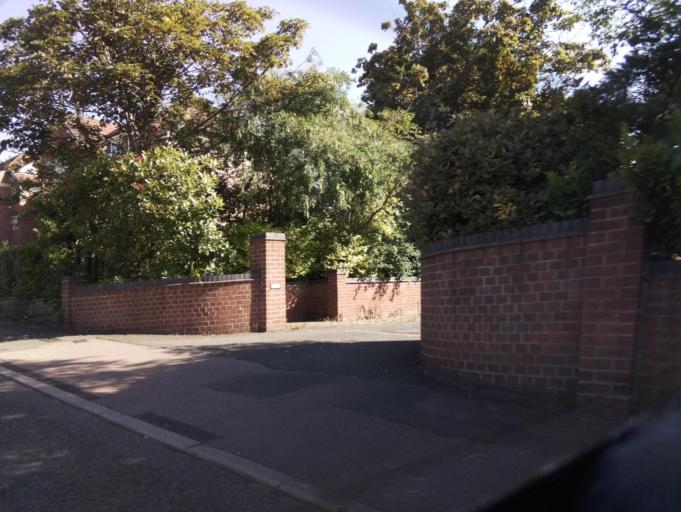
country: GB
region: England
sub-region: Derby
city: Derby
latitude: 52.9073
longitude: -1.5004
